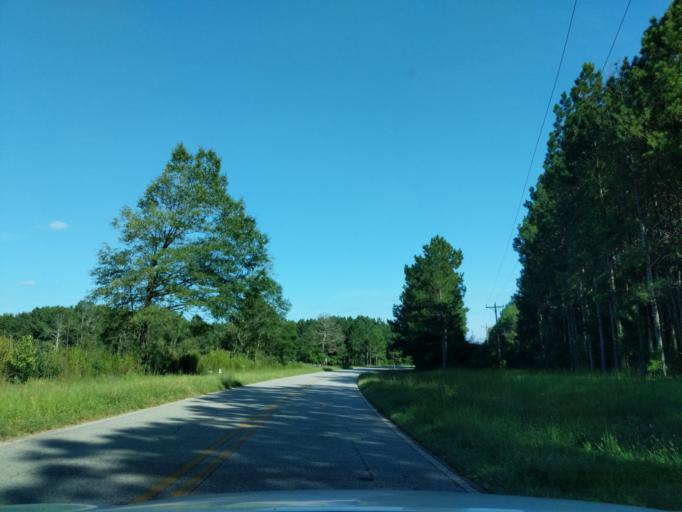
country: US
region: Georgia
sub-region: Oglethorpe County
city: Lexington
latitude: 33.9188
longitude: -83.0200
